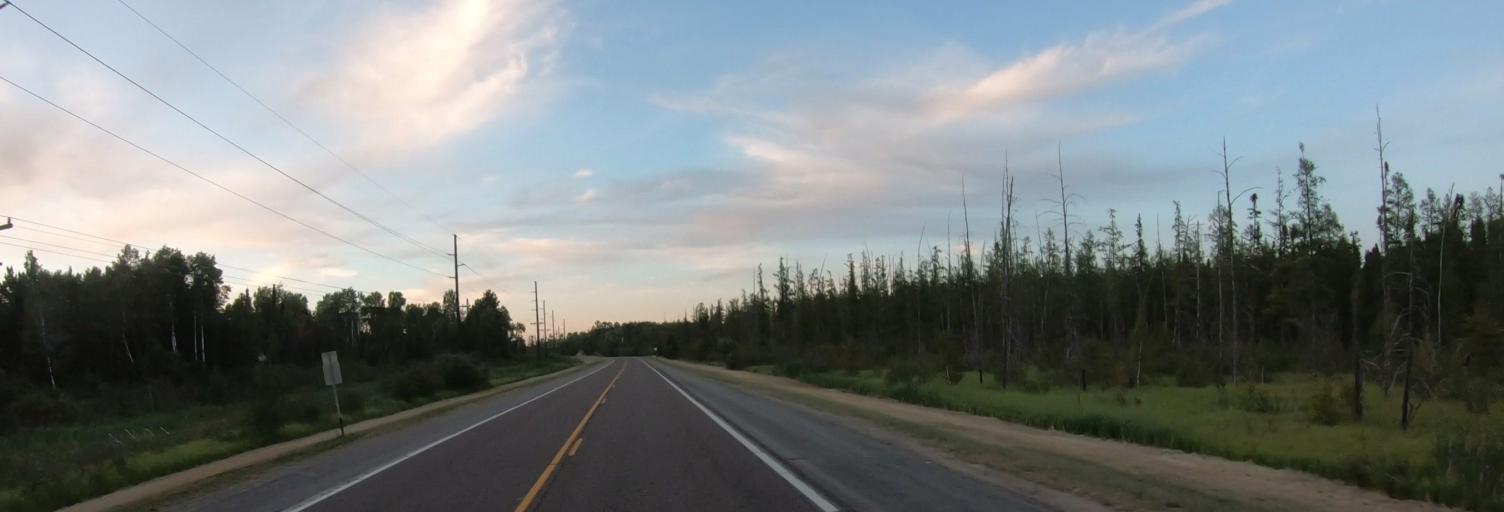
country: US
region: Minnesota
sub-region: Saint Louis County
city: Aurora
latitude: 47.8104
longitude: -92.3721
